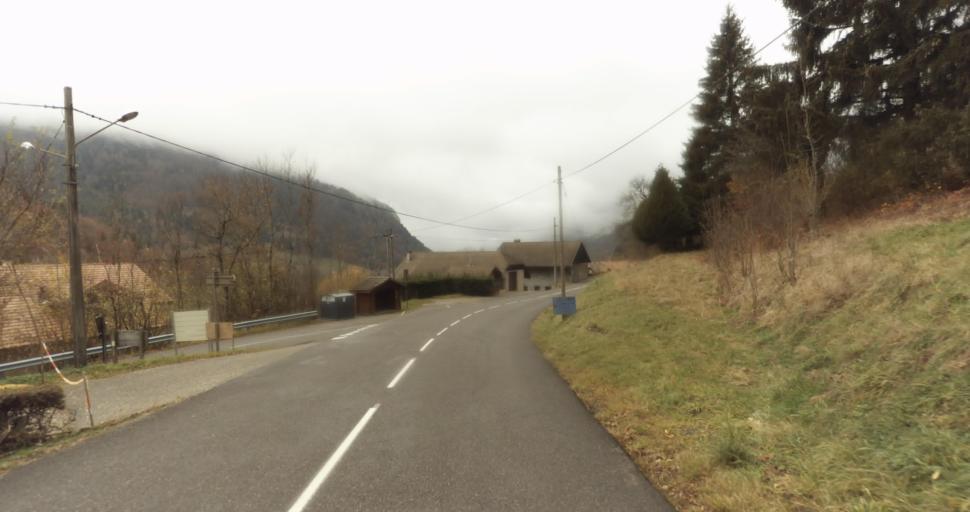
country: FR
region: Rhone-Alpes
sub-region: Departement de la Haute-Savoie
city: Thorens-Glieres
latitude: 45.9743
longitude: 6.2882
